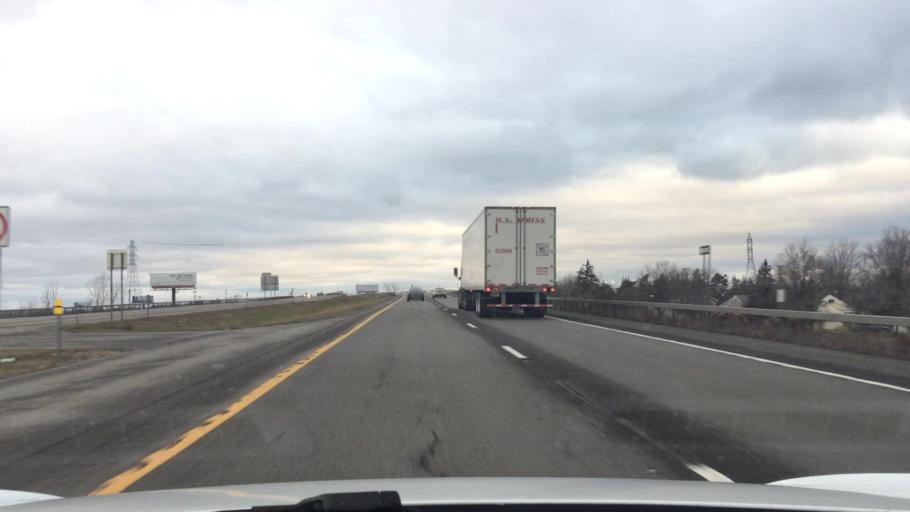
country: US
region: New York
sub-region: Niagara County
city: Niagara Falls
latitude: 43.1147
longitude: -78.9983
